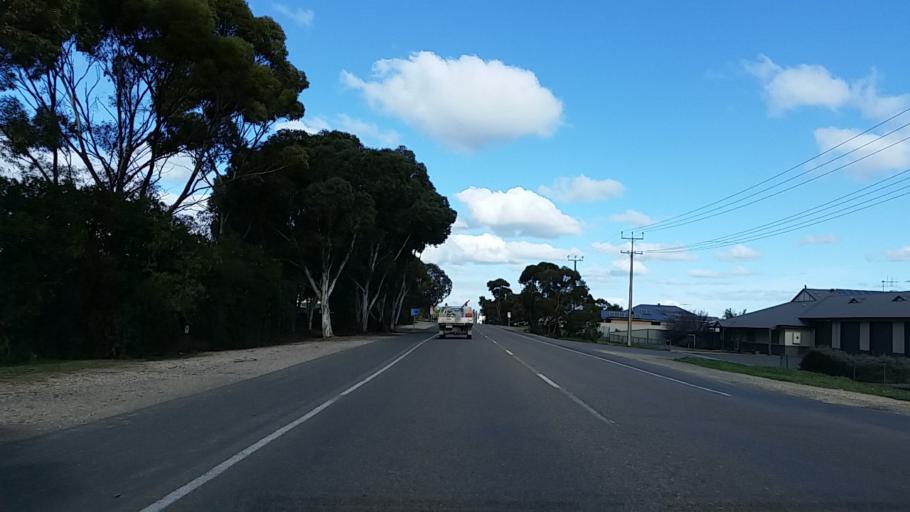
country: AU
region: South Australia
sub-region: Murray Bridge
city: Murray Bridge
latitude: -35.1440
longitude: 139.2858
